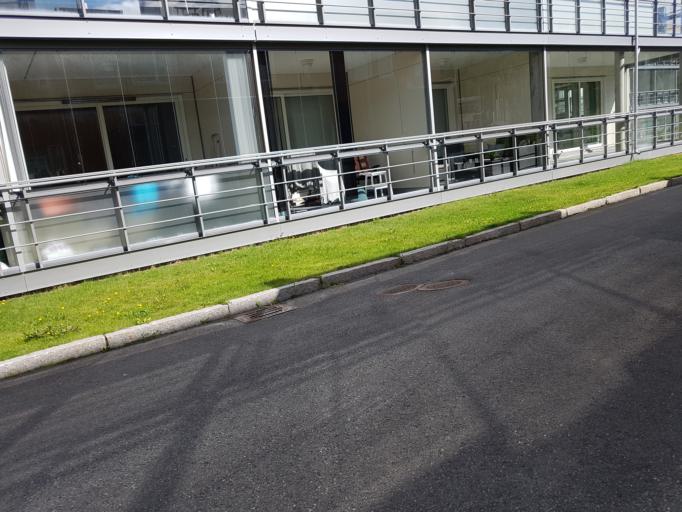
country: NO
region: Sor-Trondelag
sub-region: Trondheim
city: Trondheim
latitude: 63.4131
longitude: 10.4716
